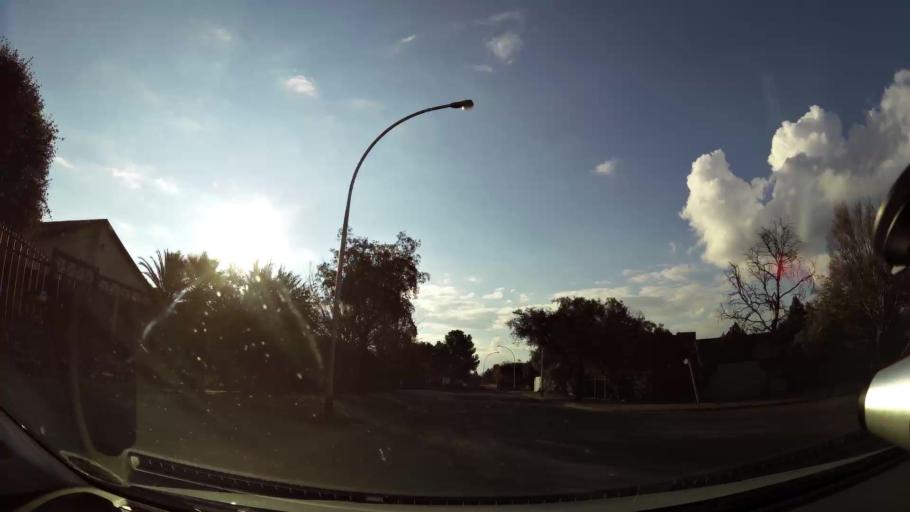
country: ZA
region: Orange Free State
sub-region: Mangaung Metropolitan Municipality
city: Bloemfontein
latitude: -29.1505
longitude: 26.1747
